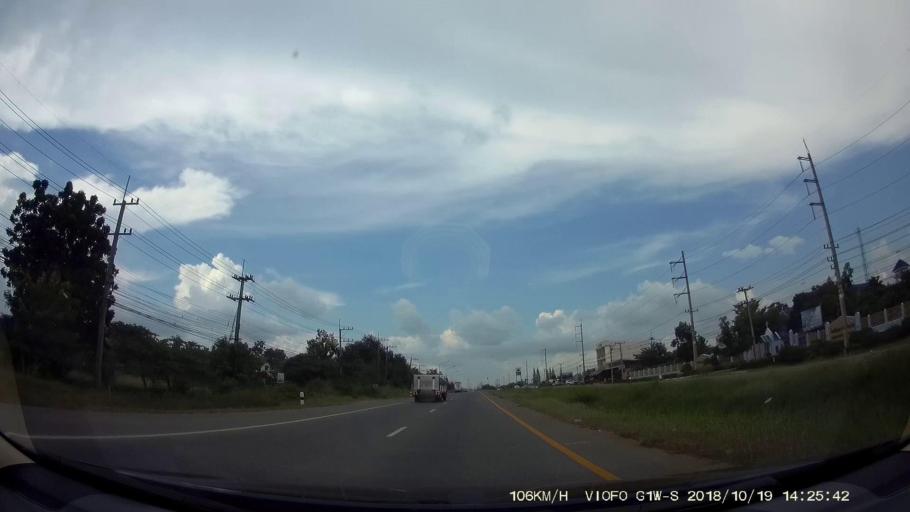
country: TH
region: Chaiyaphum
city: Kaeng Khro
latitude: 16.0974
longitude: 102.2631
